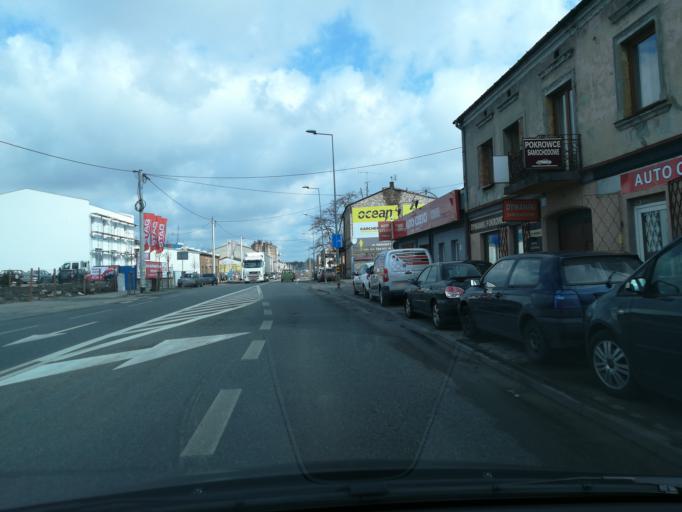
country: PL
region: Silesian Voivodeship
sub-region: Czestochowa
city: Czestochowa
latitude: 50.8190
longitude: 19.1304
